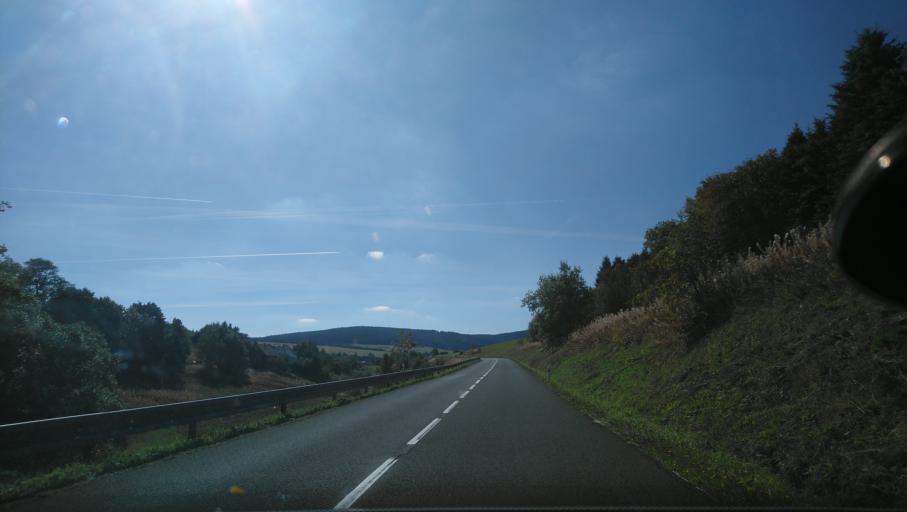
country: DE
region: Saxony
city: Kurort Oberwiesenthal
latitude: 50.4217
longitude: 12.9968
